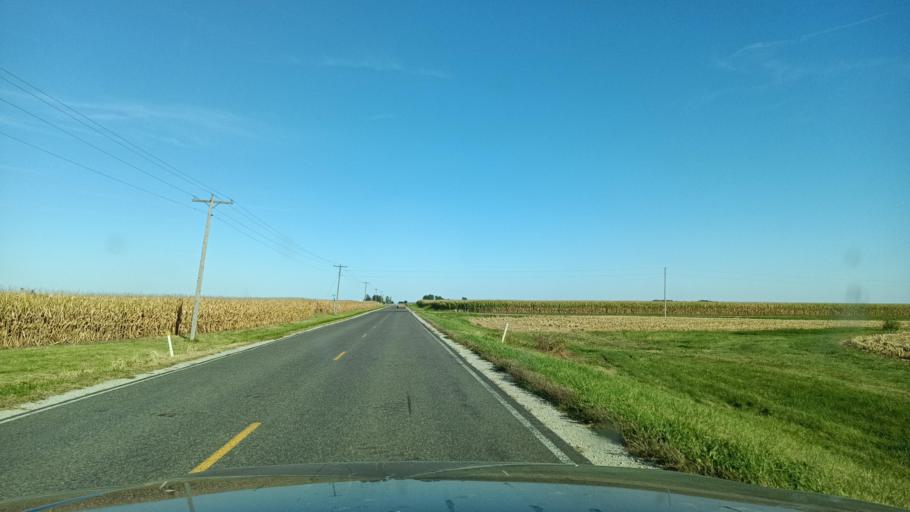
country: US
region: Illinois
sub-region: De Witt County
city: Clinton
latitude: 40.2244
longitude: -88.8890
